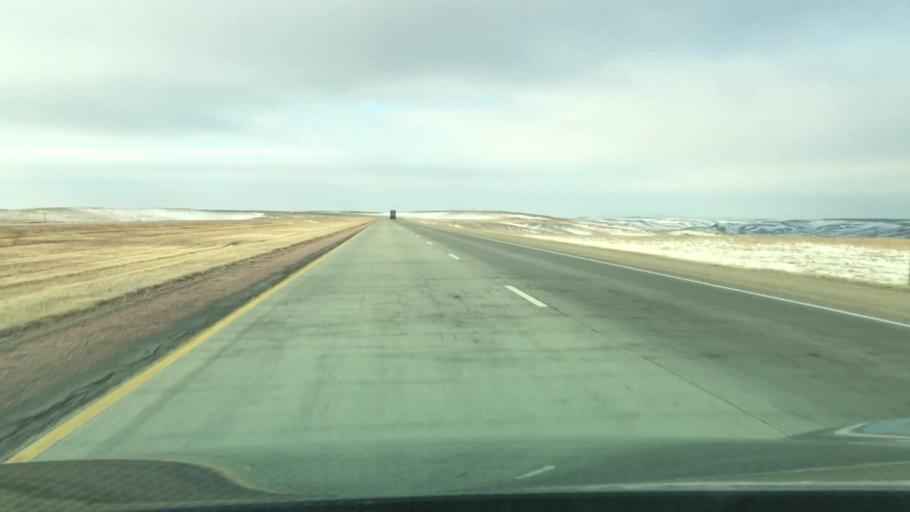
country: US
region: South Dakota
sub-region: Brule County
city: Chamberlain
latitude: 43.8390
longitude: -99.4778
